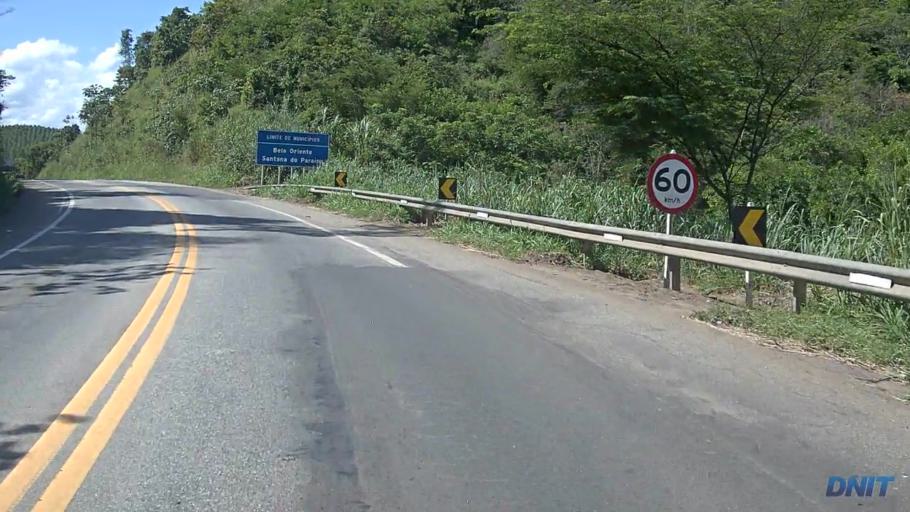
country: BR
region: Minas Gerais
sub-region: Ipaba
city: Ipaba
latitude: -19.3590
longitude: -42.4368
